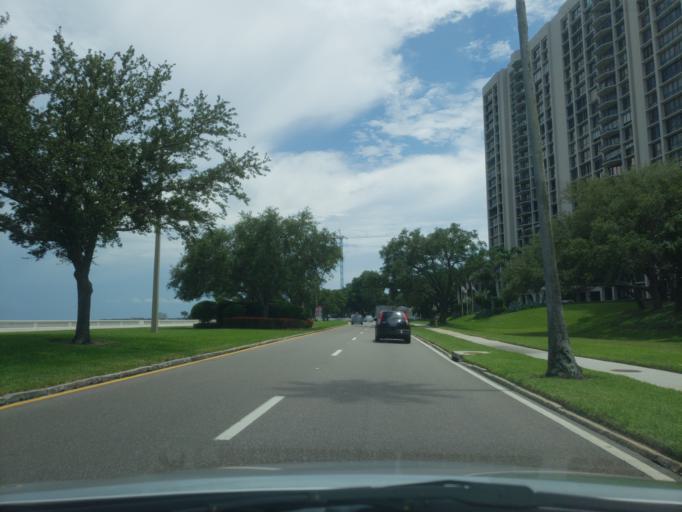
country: US
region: Florida
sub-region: Hillsborough County
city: Tampa
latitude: 27.9171
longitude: -82.4913
